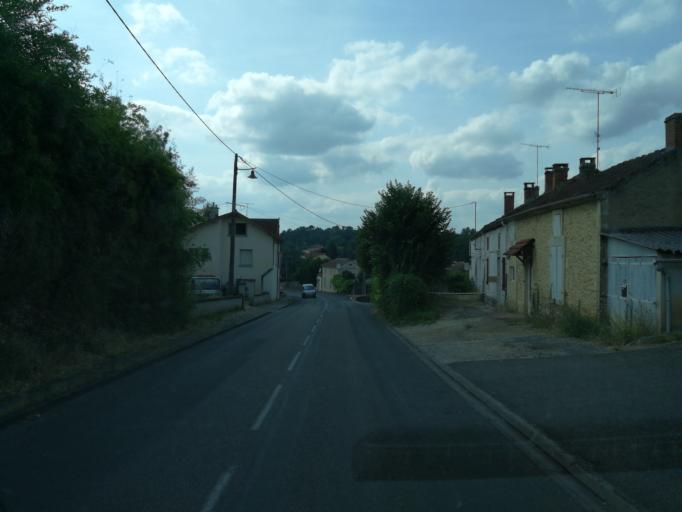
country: FR
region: Aquitaine
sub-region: Departement du Lot-et-Garonne
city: Fumel
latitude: 44.5023
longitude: 0.9626
